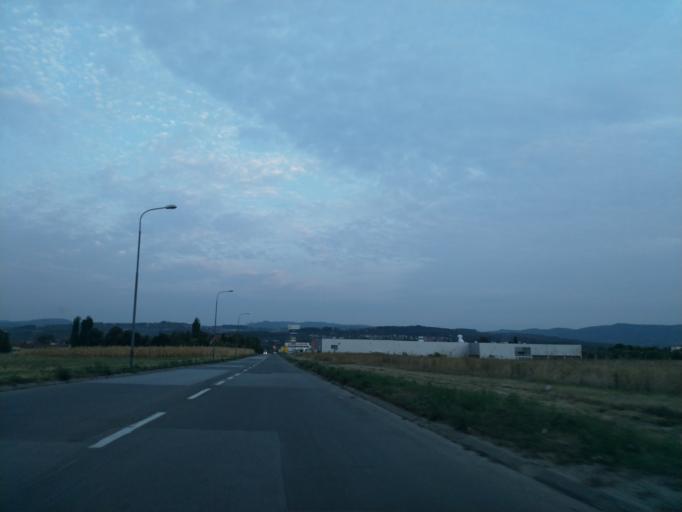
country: RS
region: Central Serbia
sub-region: Sumadijski Okrug
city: Kragujevac
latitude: 44.0267
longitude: 20.9231
